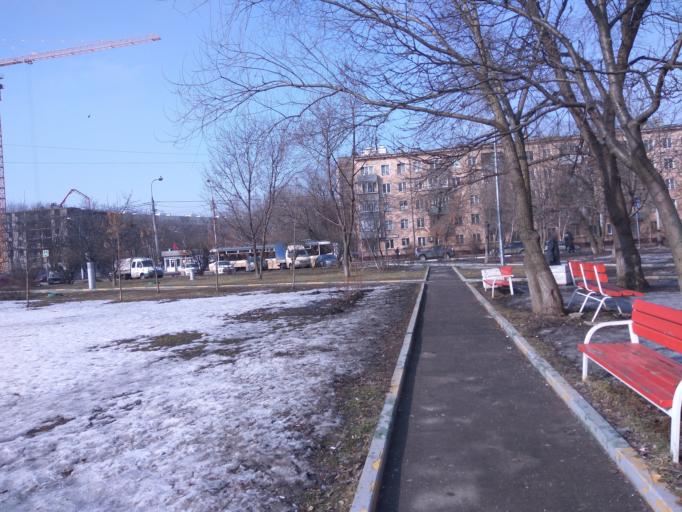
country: RU
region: Moscow
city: Kolomenskoye
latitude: 55.6810
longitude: 37.6770
